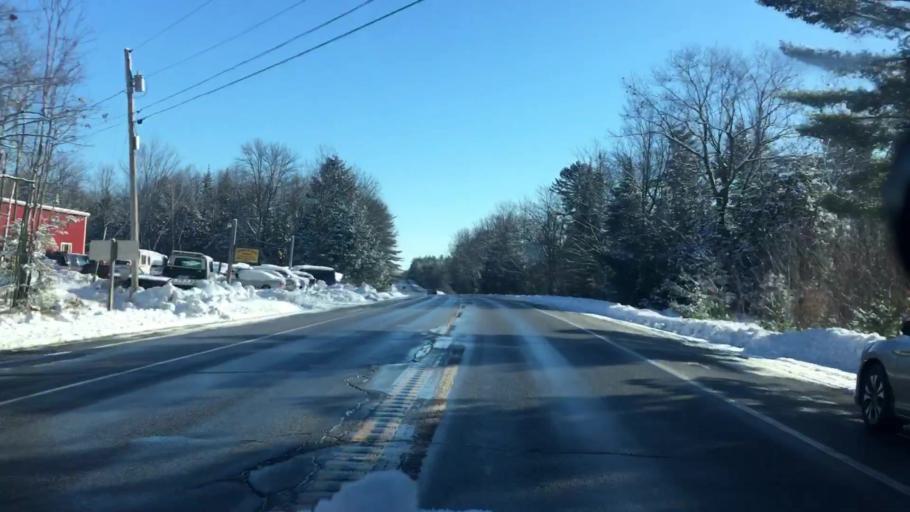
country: US
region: Maine
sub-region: Cumberland County
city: Bridgton
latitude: 44.0088
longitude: -70.6760
